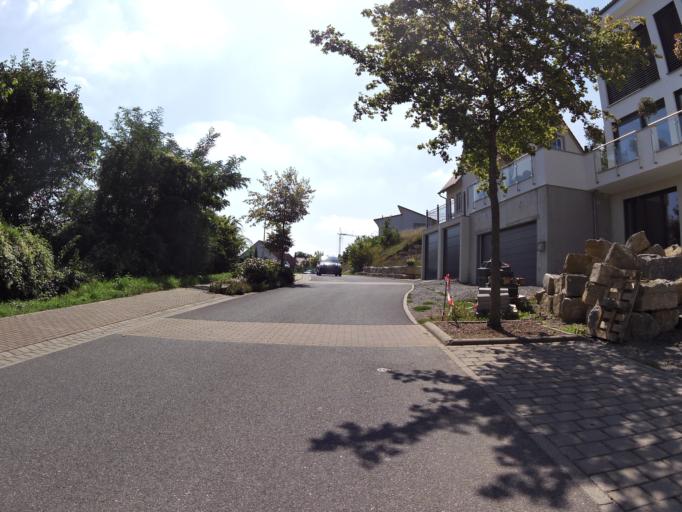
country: DE
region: Bavaria
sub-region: Regierungsbezirk Unterfranken
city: Erlabrunn
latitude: 49.8626
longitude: 9.8392
